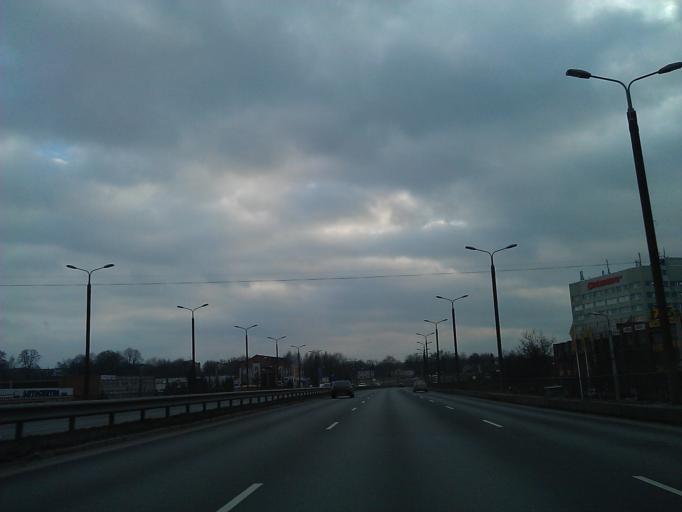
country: LV
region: Riga
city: Riga
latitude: 56.9231
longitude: 24.1043
